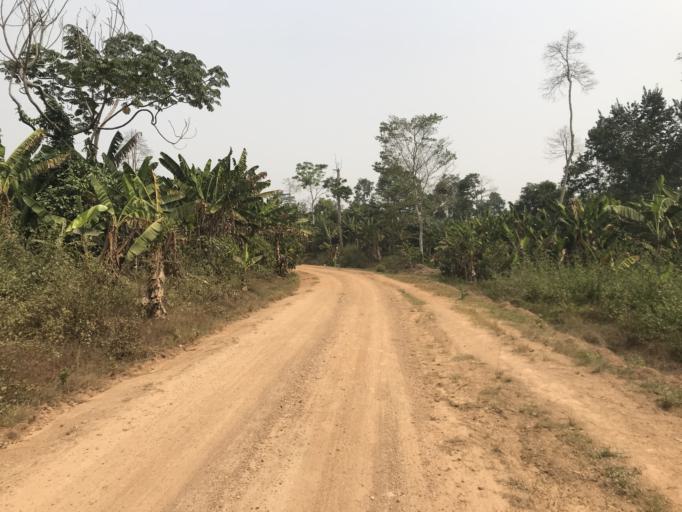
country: NG
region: Osun
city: Ifetedo
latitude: 7.0267
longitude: 4.4470
